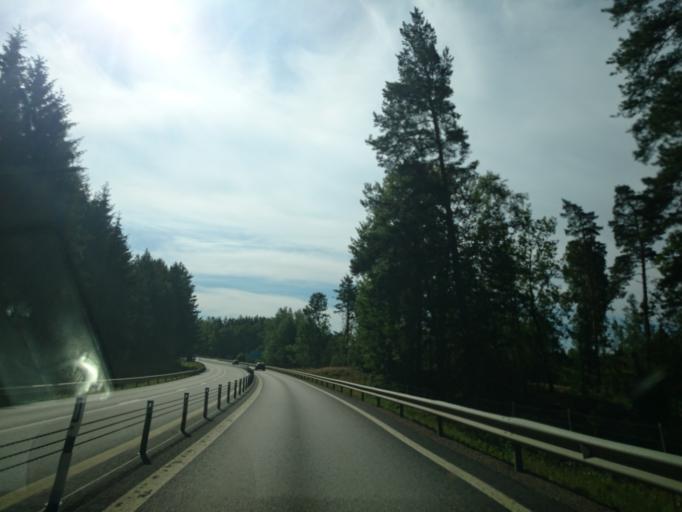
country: SE
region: Kalmar
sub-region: Vasterviks Kommun
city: Gamleby
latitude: 57.8278
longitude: 16.4469
